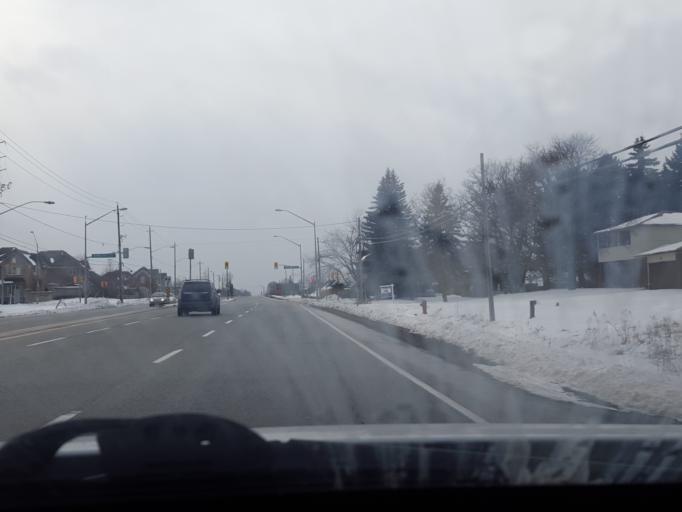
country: CA
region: Ontario
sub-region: York
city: Richmond Hill
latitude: 43.9407
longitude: -79.4736
